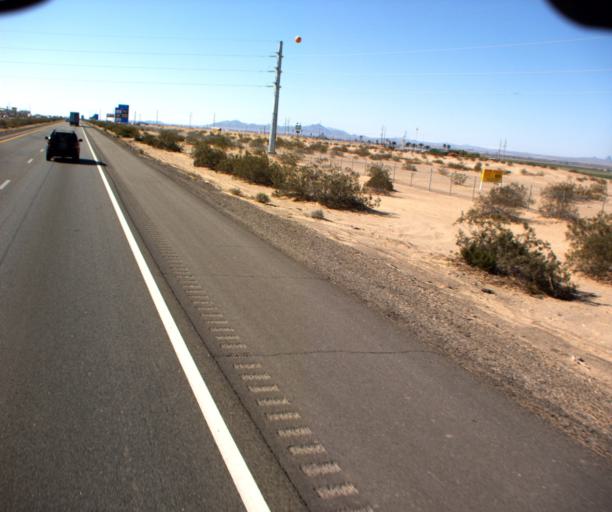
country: US
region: Arizona
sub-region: Yuma County
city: Yuma
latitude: 32.6810
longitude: -114.5534
